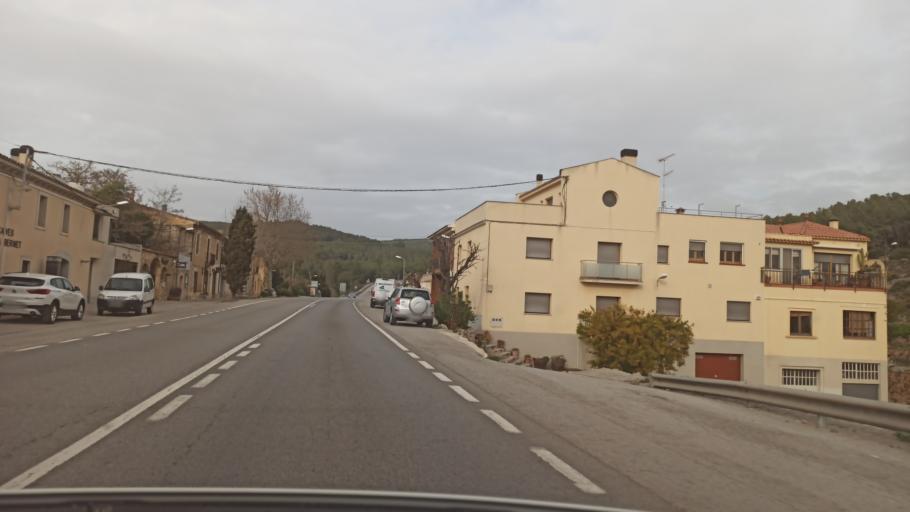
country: ES
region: Catalonia
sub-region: Provincia de Barcelona
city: Subirats
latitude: 41.3847
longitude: 1.8134
